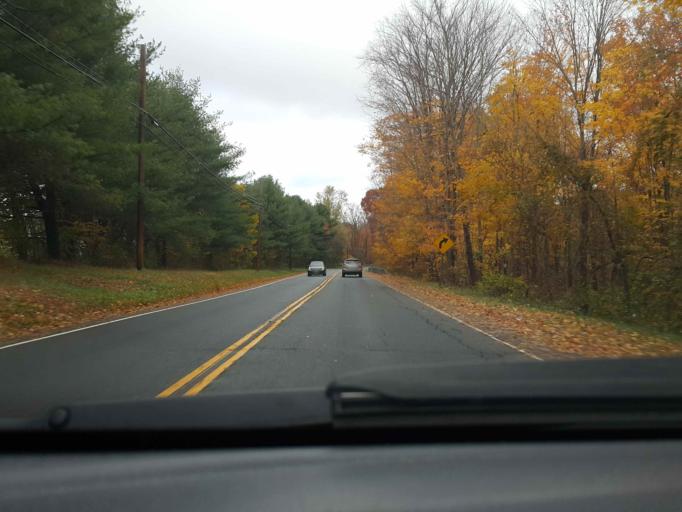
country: US
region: Connecticut
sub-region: Middlesex County
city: Durham
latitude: 41.5183
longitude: -72.6685
